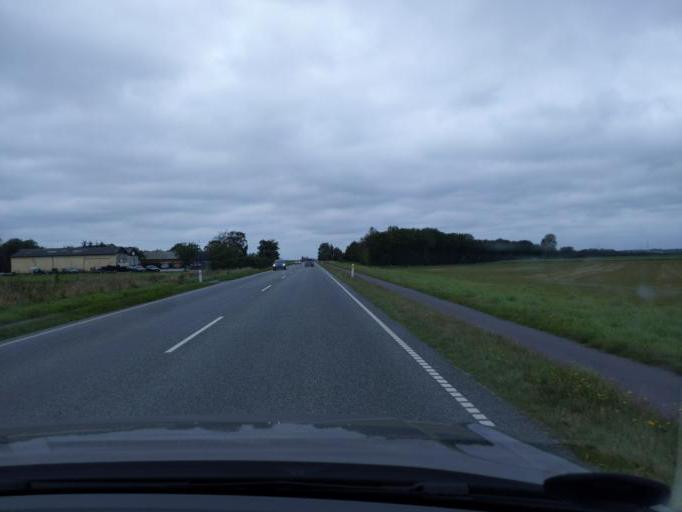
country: DK
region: Central Jutland
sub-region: Randers Kommune
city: Randers
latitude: 56.4955
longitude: 9.9728
